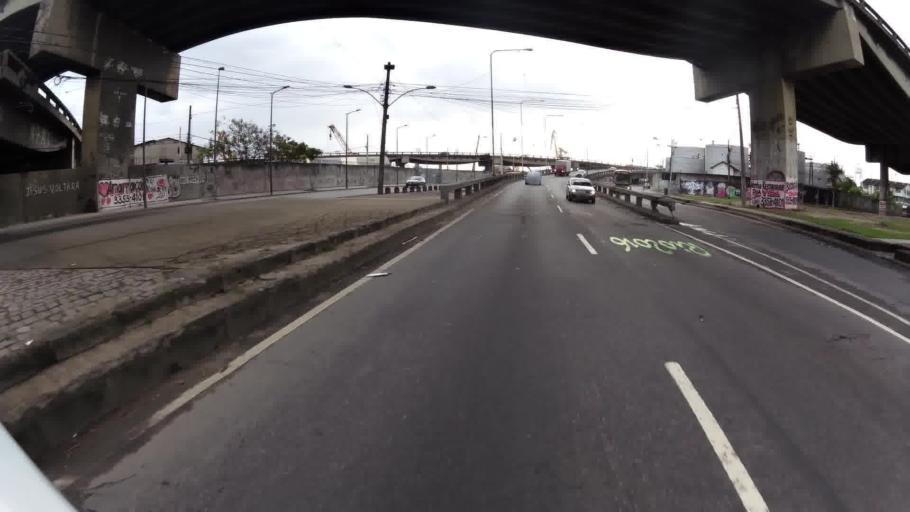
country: BR
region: Rio de Janeiro
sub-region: Rio De Janeiro
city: Rio de Janeiro
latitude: -22.8888
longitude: -43.2182
